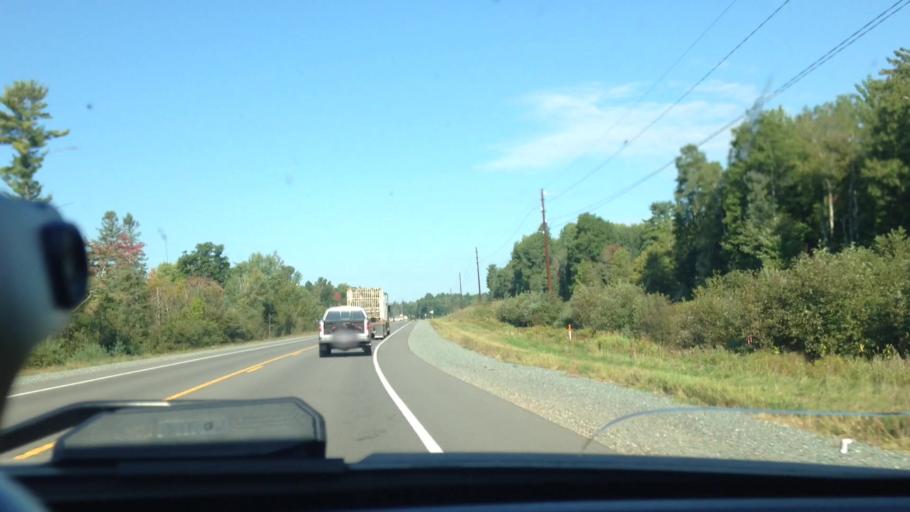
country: US
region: Michigan
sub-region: Dickinson County
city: Iron Mountain
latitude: 45.8770
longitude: -88.1177
